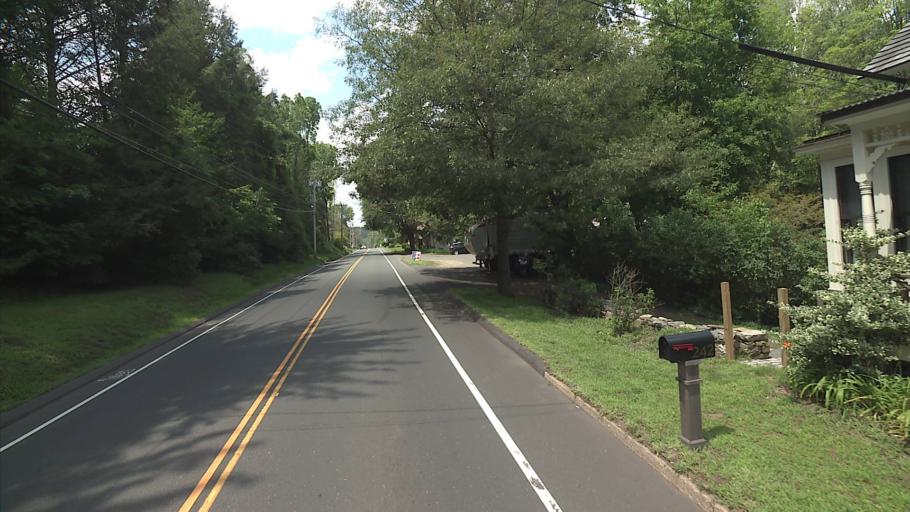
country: US
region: Connecticut
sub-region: Middlesex County
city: Higganum
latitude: 41.4986
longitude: -72.5639
